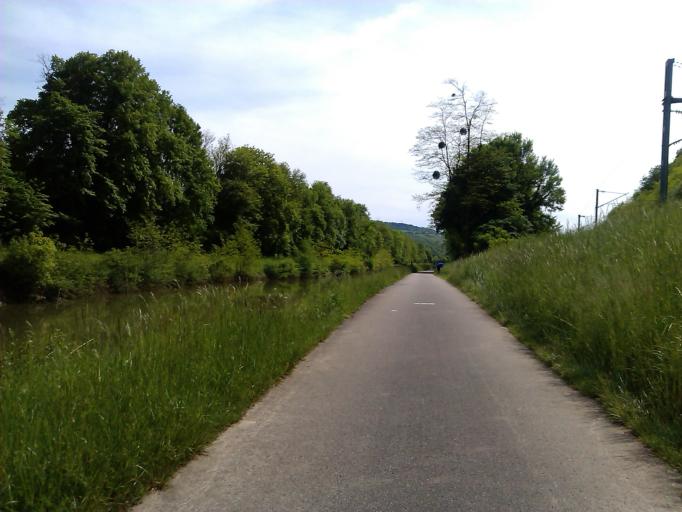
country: FR
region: Franche-Comte
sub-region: Departement du Doubs
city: Boussieres
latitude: 47.1558
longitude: 5.8835
